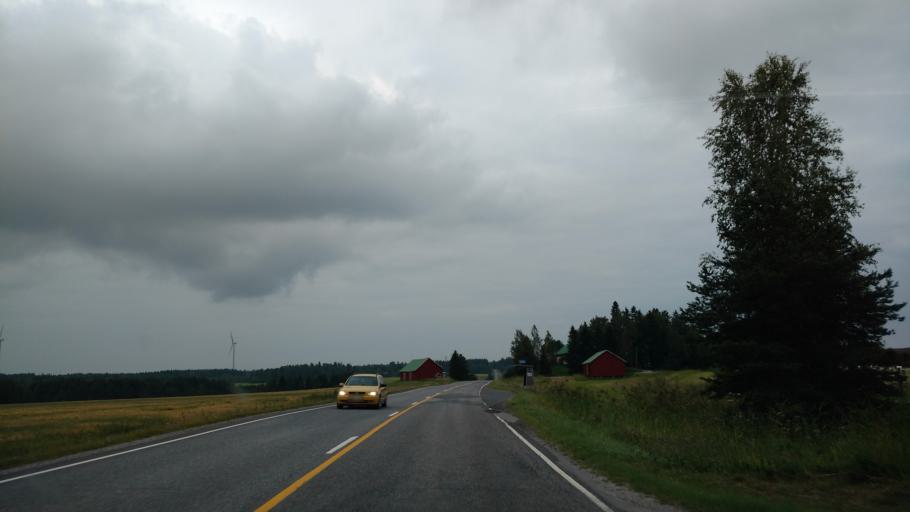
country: FI
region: Varsinais-Suomi
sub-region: Salo
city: Halikko
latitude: 60.4766
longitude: 23.0120
